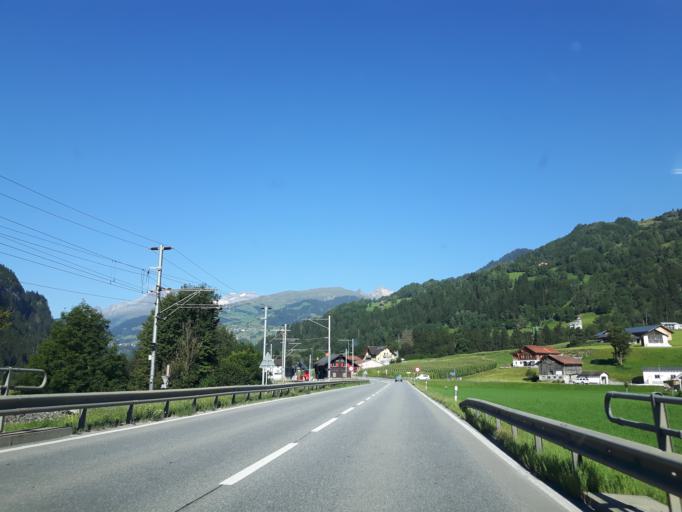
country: CH
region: Grisons
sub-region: Surselva District
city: Ilanz
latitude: 46.7740
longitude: 9.1798
